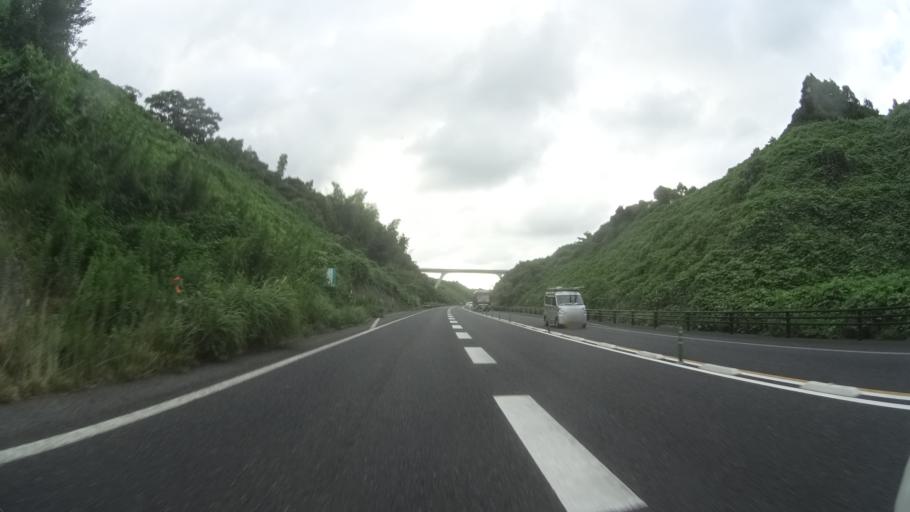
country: JP
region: Tottori
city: Kurayoshi
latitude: 35.4864
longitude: 133.6810
